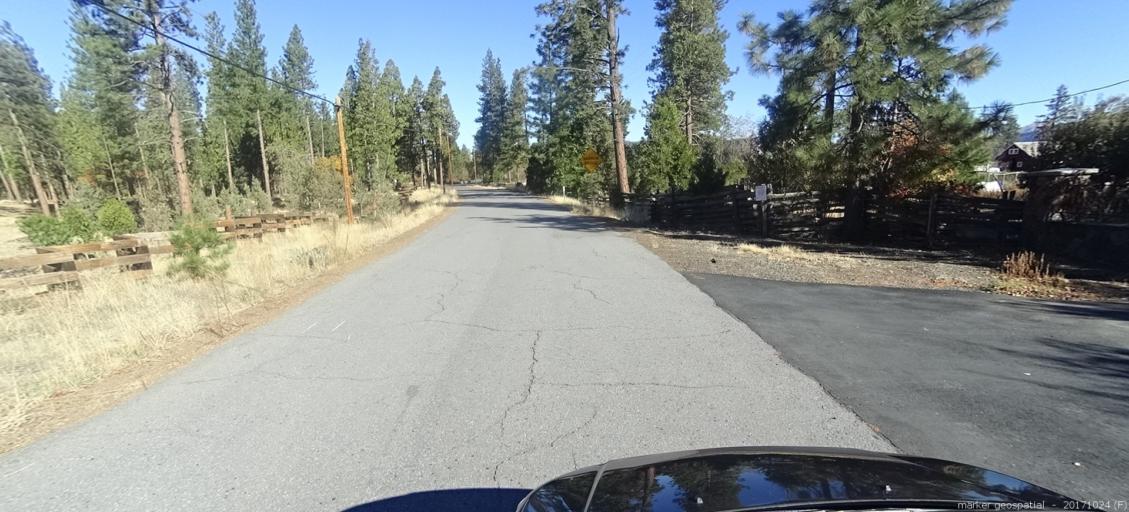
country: US
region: California
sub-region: Shasta County
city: Burney
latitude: 40.8148
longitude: -121.5040
